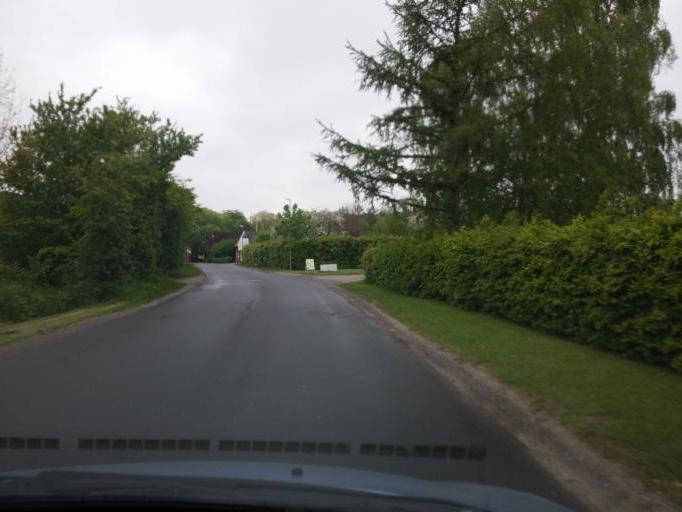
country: DK
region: South Denmark
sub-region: Odense Kommune
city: Bullerup
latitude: 55.4094
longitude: 10.5090
